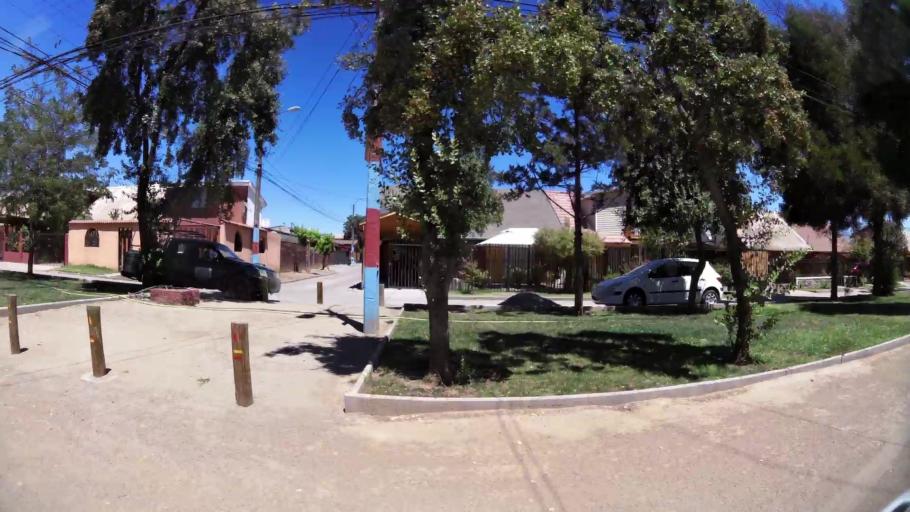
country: CL
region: O'Higgins
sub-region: Provincia de Cachapoal
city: Rancagua
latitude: -34.1585
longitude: -70.7053
